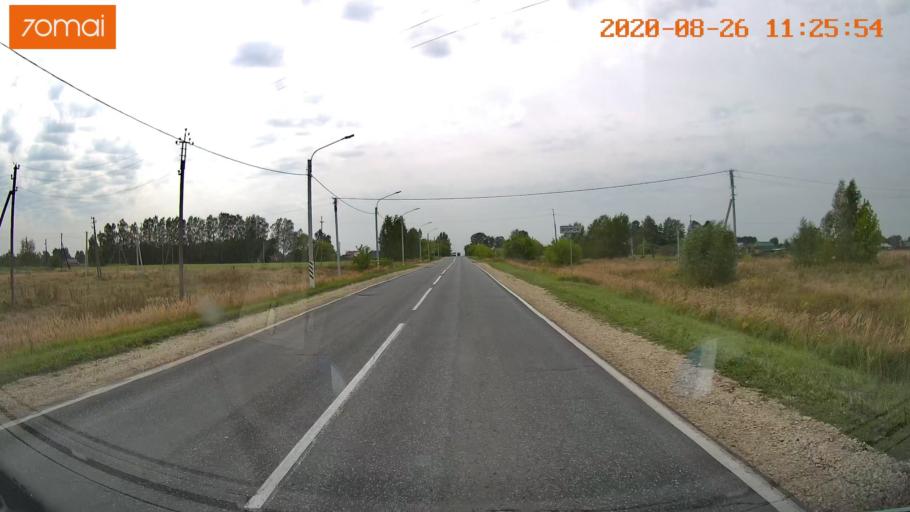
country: RU
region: Rjazan
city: Shilovo
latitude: 54.3378
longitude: 40.9564
